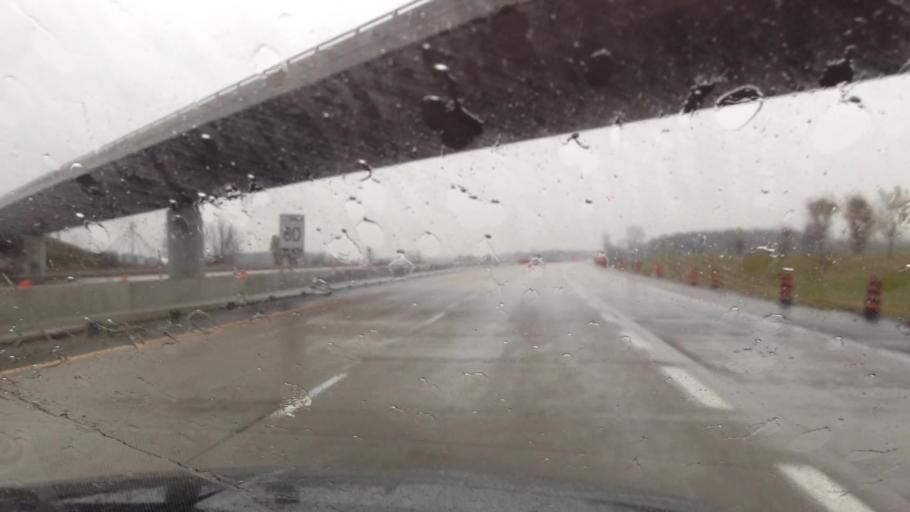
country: CA
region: Ontario
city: Hawkesbury
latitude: 45.4671
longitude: -74.6806
